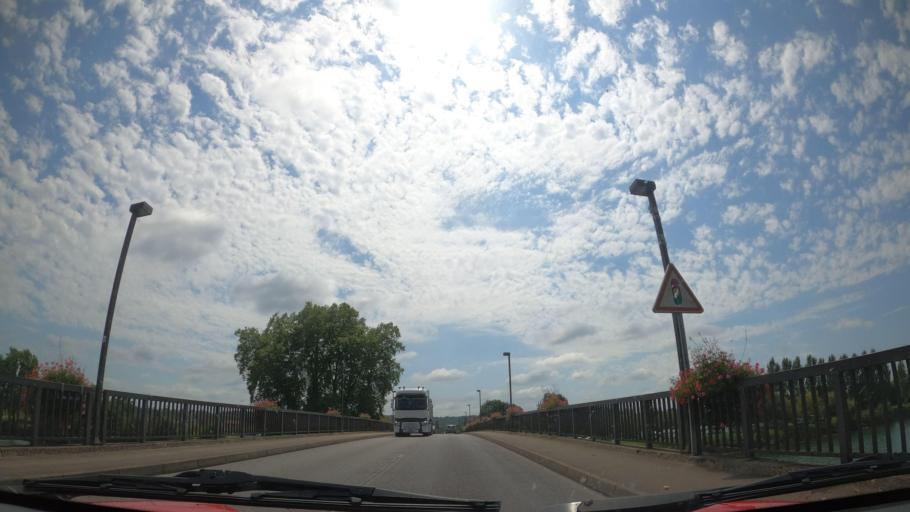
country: FR
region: Aquitaine
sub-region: Departement des Landes
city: Peyrehorade
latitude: 43.5436
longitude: -1.1055
